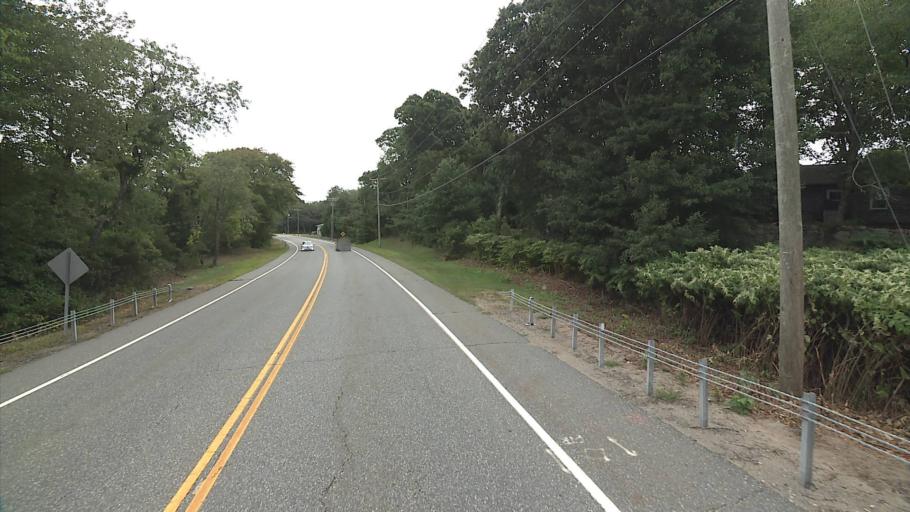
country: US
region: Connecticut
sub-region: Middlesex County
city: Old Saybrook Center
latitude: 41.2870
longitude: -72.3091
